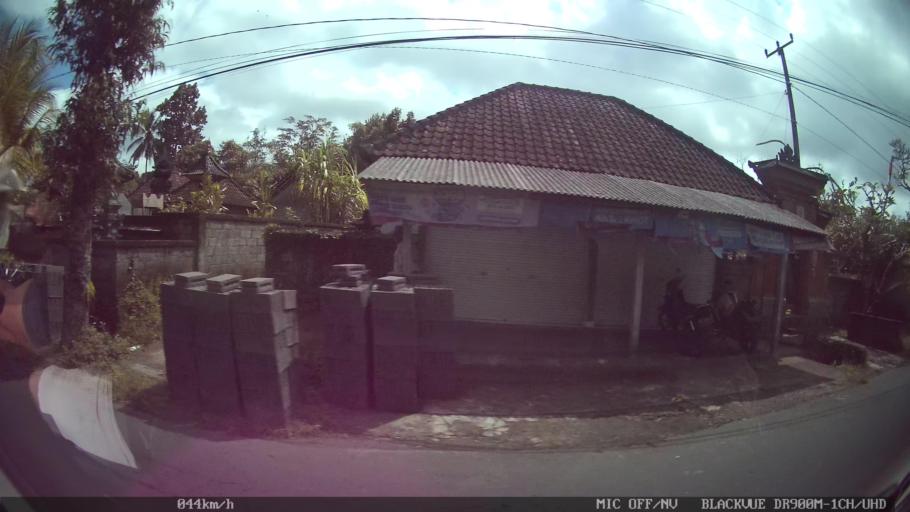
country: ID
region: Bali
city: Banjar Mulung
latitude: -8.4917
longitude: 115.3207
